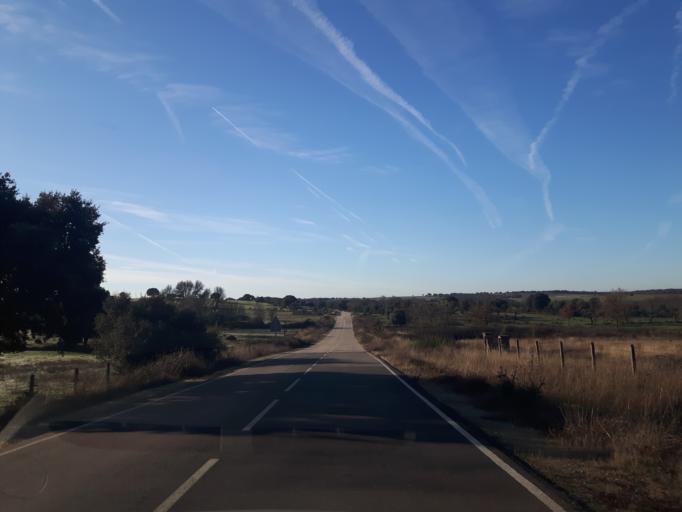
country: ES
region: Castille and Leon
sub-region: Provincia de Salamanca
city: Olmedo de Camaces
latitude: 40.8938
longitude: -6.6206
